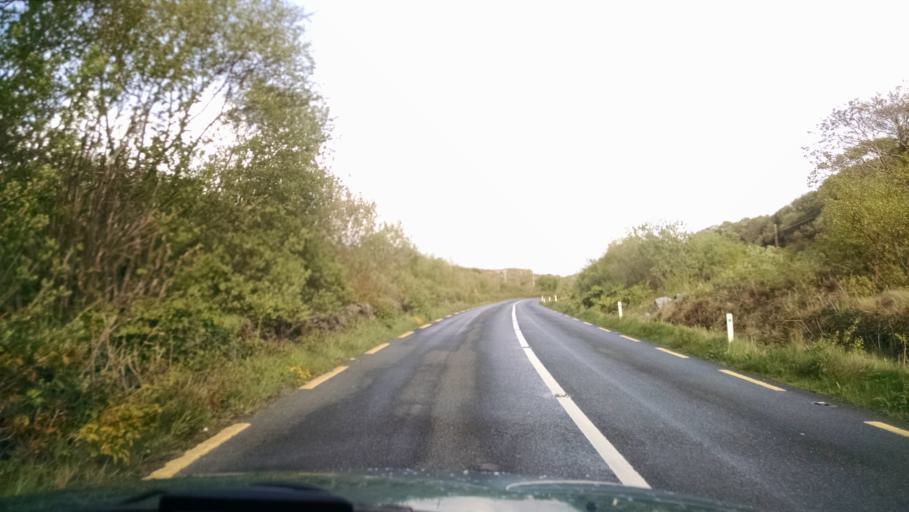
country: IE
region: Connaught
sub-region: County Galway
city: Clifden
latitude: 53.4857
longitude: -9.9837
